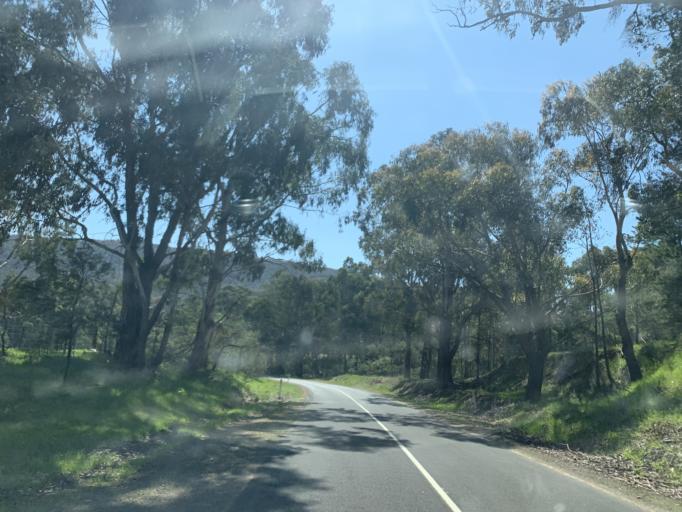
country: AU
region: Victoria
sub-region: Benalla
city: Benalla
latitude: -36.7685
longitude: 146.1393
